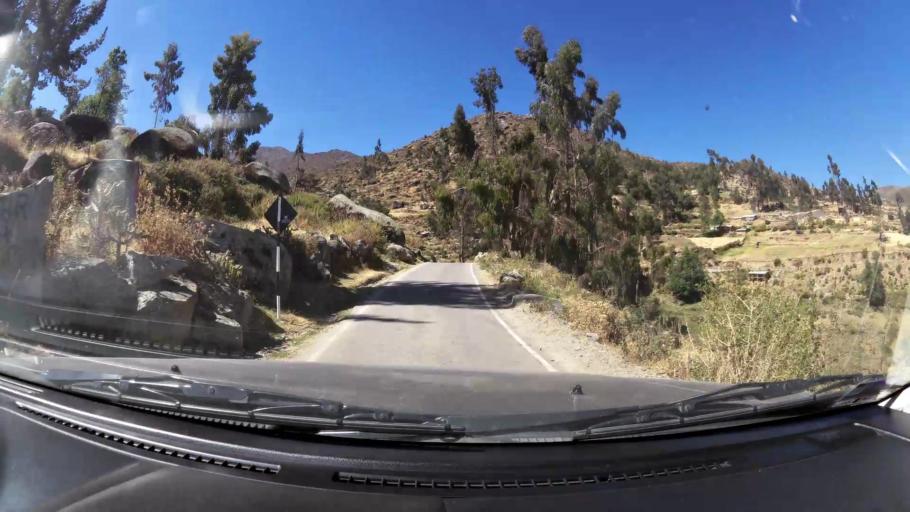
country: PE
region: Huancavelica
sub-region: Huaytara
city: Quito-Arma
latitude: -13.6840
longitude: -75.3759
